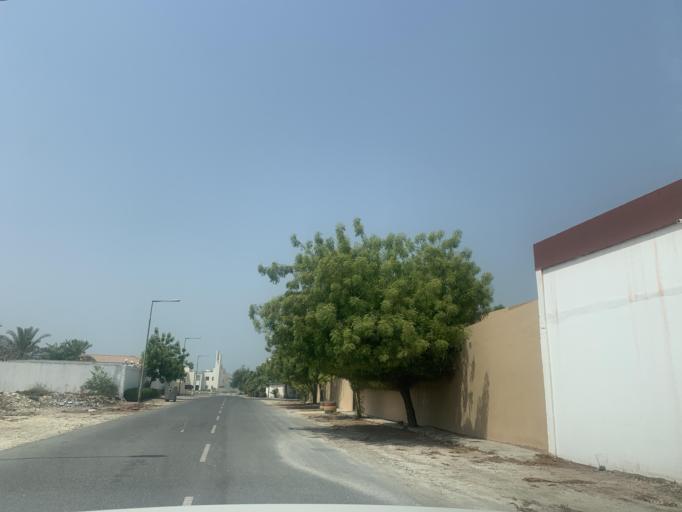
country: BH
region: Central Governorate
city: Madinat Hamad
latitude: 26.1465
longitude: 50.4753
